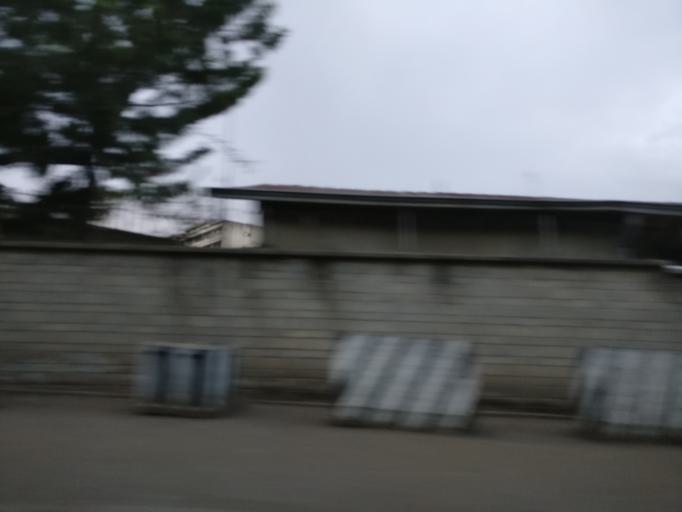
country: ET
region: Adis Abeba
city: Addis Ababa
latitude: 9.0173
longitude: 38.7533
